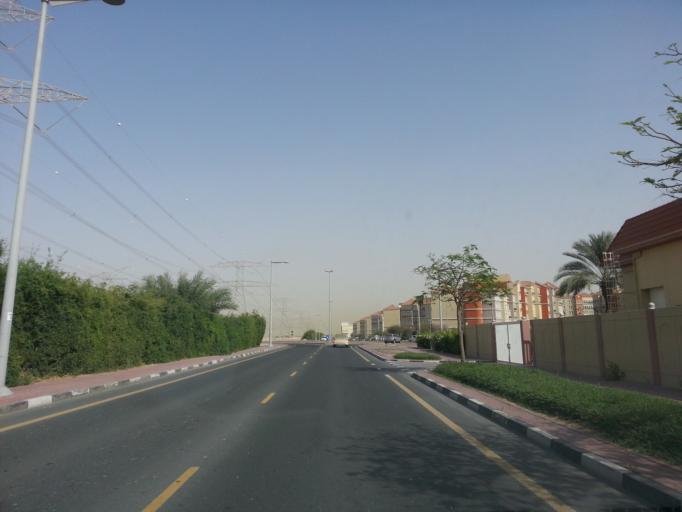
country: AE
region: Dubai
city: Dubai
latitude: 25.0412
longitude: 55.1462
